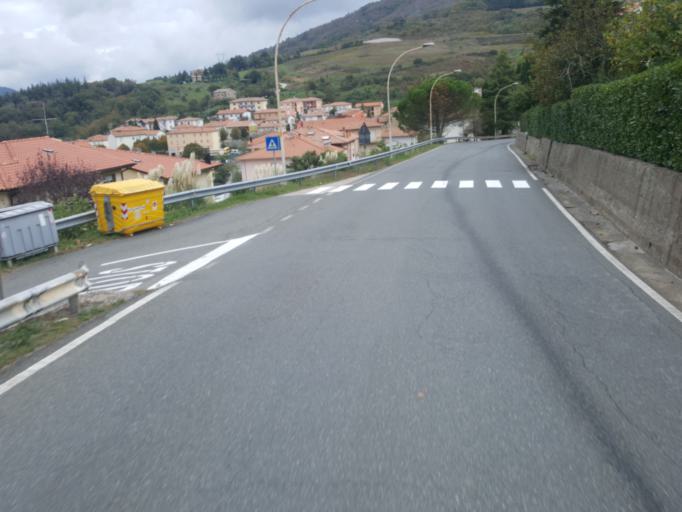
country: IT
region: Tuscany
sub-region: Province of Pisa
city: Castelnuovo di Val di Cecina
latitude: 43.2137
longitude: 10.8997
